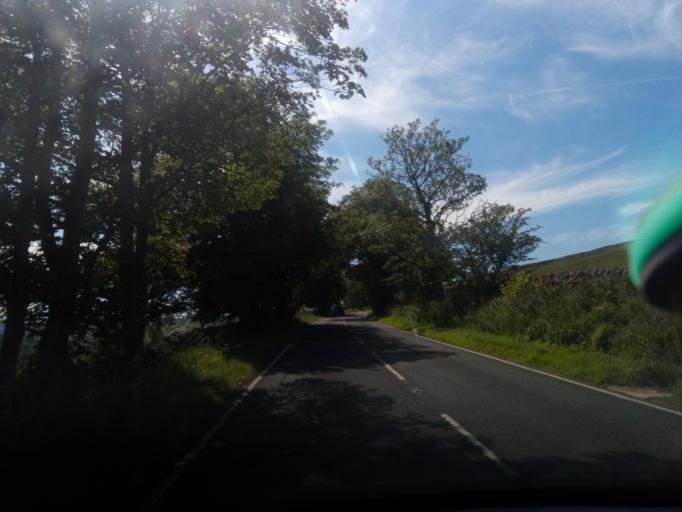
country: GB
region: England
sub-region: Northumberland
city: Bardon Mill
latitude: 54.8816
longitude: -2.3507
